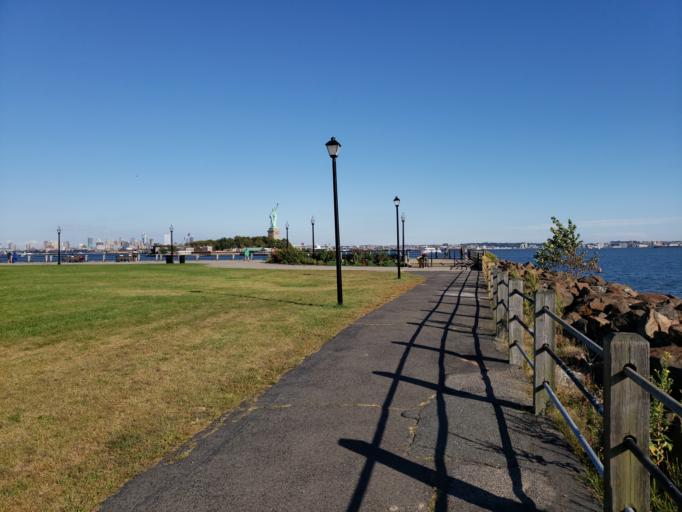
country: US
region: New Jersey
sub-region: Hudson County
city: Jersey City
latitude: 40.6911
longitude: -74.0556
